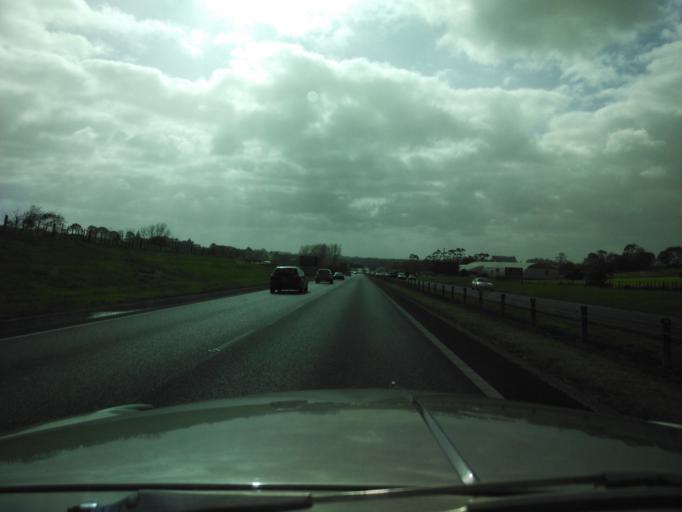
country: NZ
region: Auckland
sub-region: Auckland
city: Rothesay Bay
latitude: -36.6365
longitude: 174.6627
